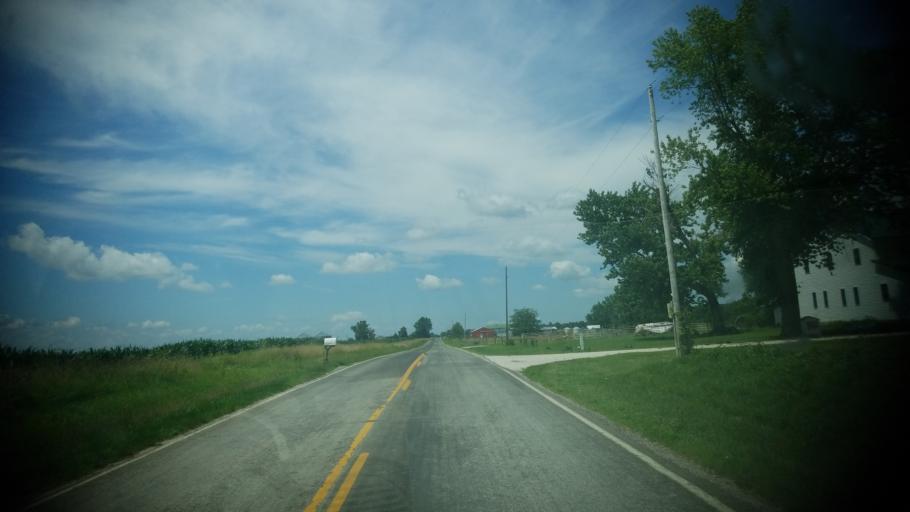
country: US
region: Missouri
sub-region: Audrain County
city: Vandalia
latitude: 39.3248
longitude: -91.3451
